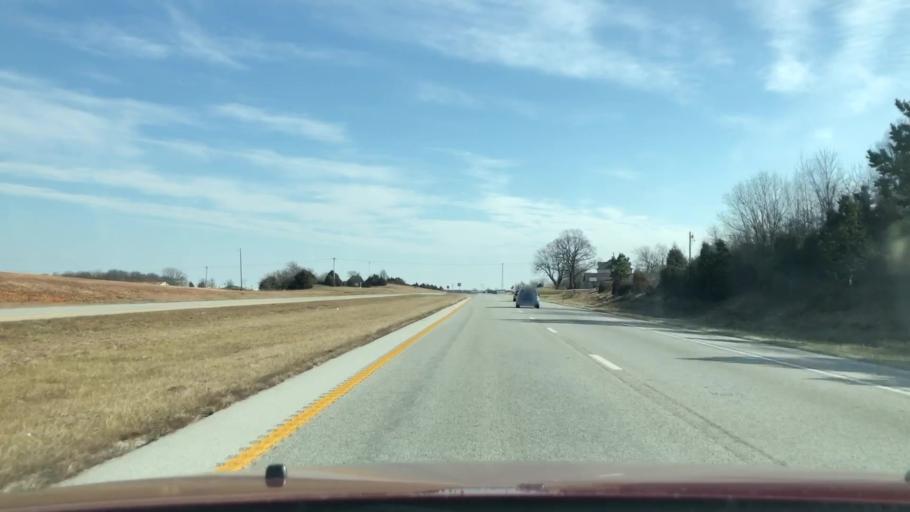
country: US
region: Missouri
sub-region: Webster County
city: Seymour
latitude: 37.1564
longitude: -92.7753
